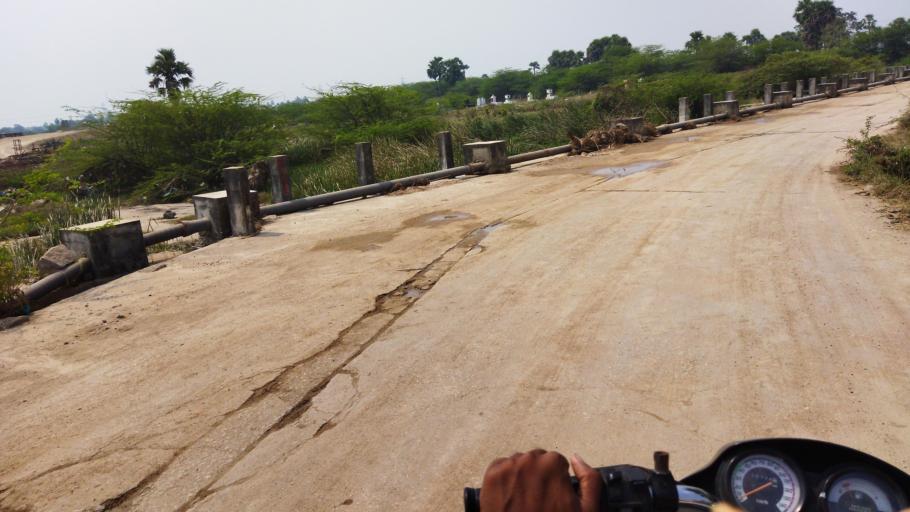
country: IN
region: Telangana
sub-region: Nalgonda
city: Nalgonda
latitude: 17.1403
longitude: 79.3879
